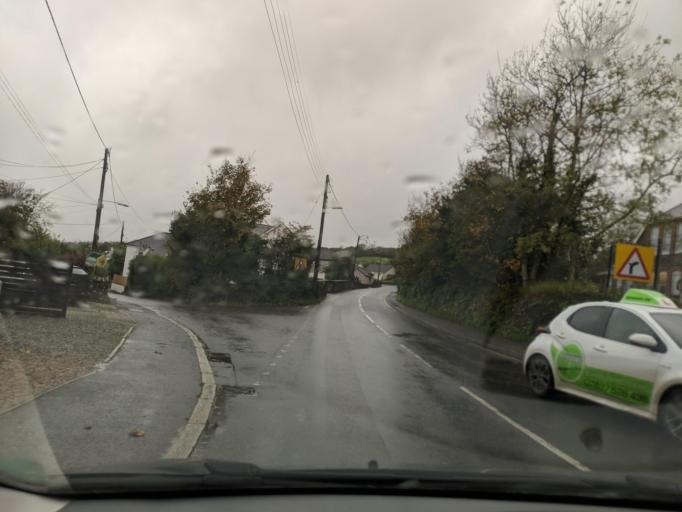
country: GB
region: England
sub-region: Cornwall
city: Bodmin
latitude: 50.4639
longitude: -4.7161
